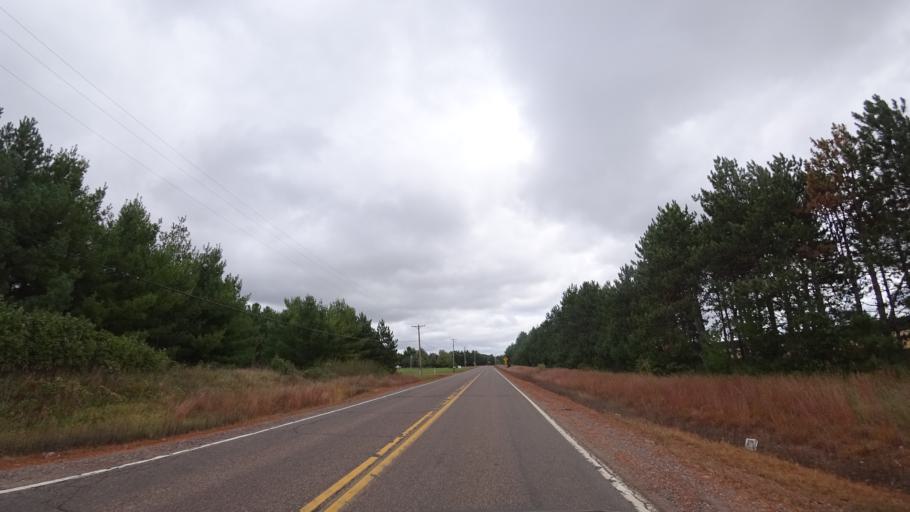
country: US
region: Wisconsin
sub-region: Chippewa County
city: Lake Wissota
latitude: 44.9446
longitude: -91.2667
